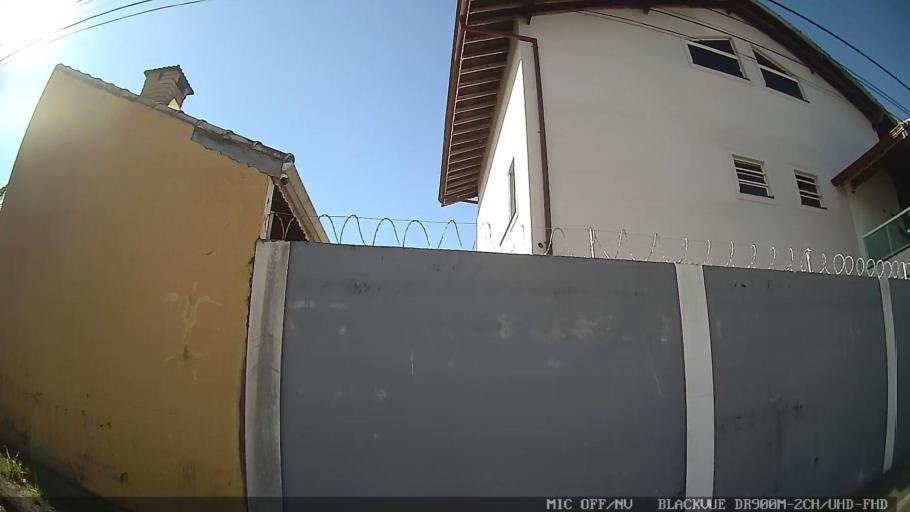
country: BR
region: Sao Paulo
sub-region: Peruibe
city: Peruibe
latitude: -24.2744
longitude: -46.9465
